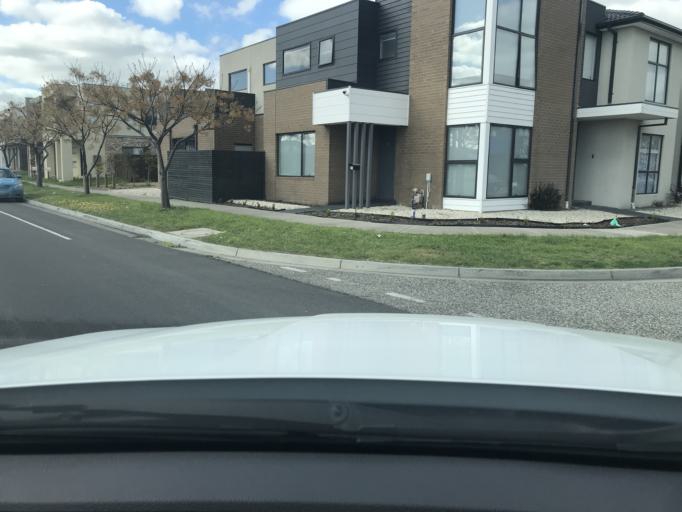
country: AU
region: Victoria
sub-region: Hume
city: Craigieburn
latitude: -37.5914
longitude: 144.9170
